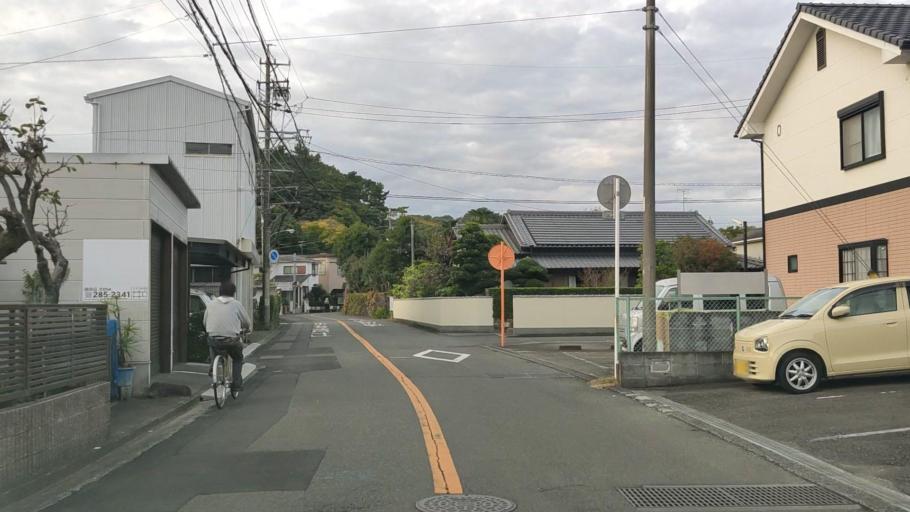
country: JP
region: Shizuoka
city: Shizuoka-shi
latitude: 34.9653
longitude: 138.4056
